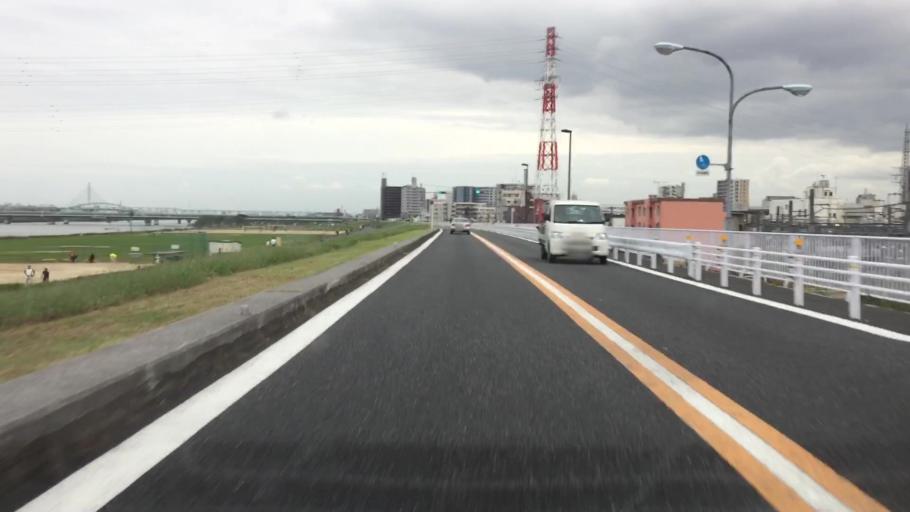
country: JP
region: Saitama
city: Soka
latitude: 35.7372
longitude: 139.8213
